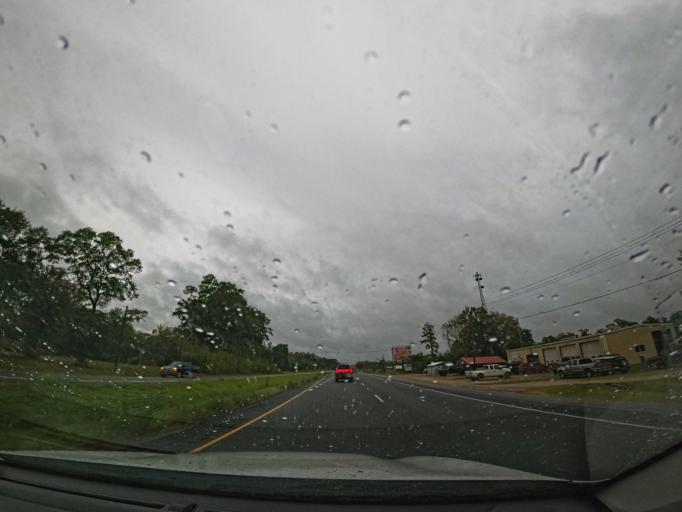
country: US
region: Texas
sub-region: Angelina County
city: Diboll
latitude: 31.2054
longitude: -94.7764
